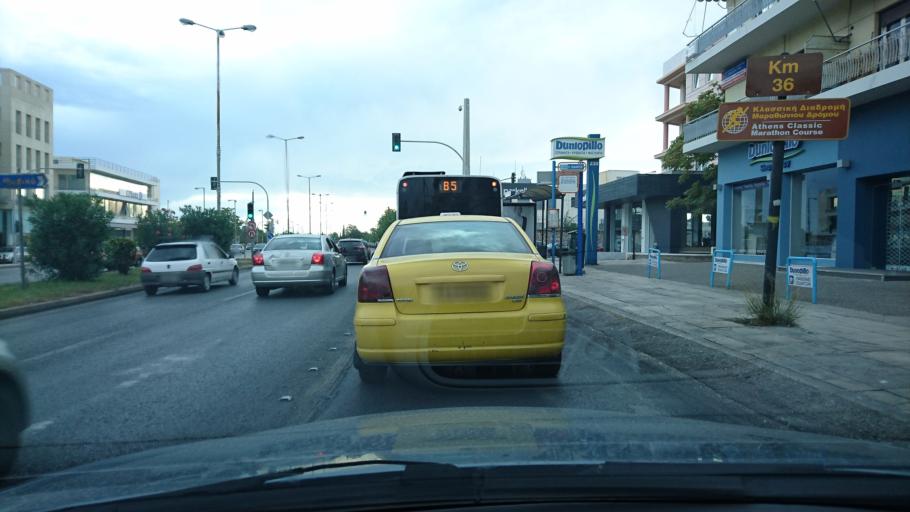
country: GR
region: Attica
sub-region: Nomarchia Athinas
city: Neo Psychiko
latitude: 38.0012
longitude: 23.7875
